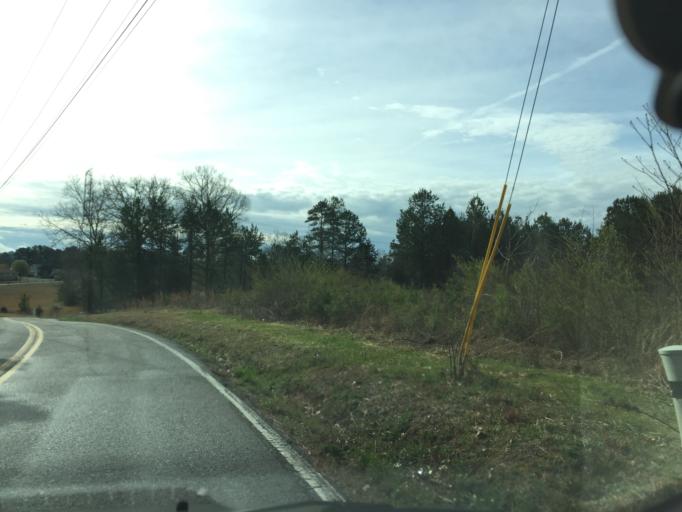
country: US
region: Tennessee
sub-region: Hamilton County
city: Collegedale
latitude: 35.0584
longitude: -85.1016
